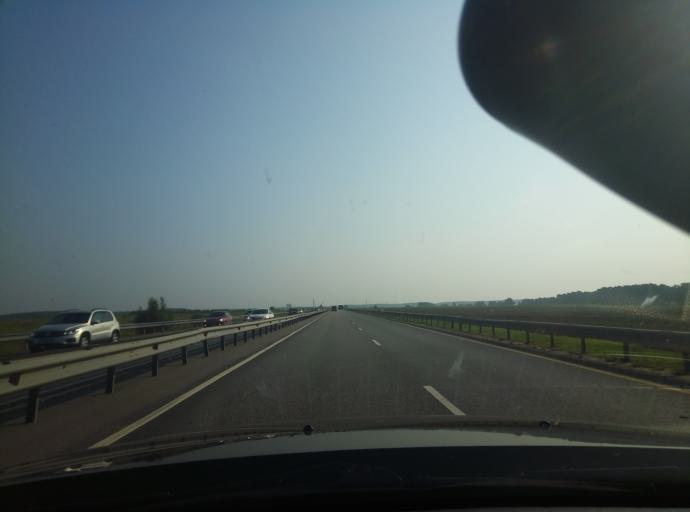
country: RU
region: Kaluga
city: Obninsk
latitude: 55.0324
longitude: 36.5806
